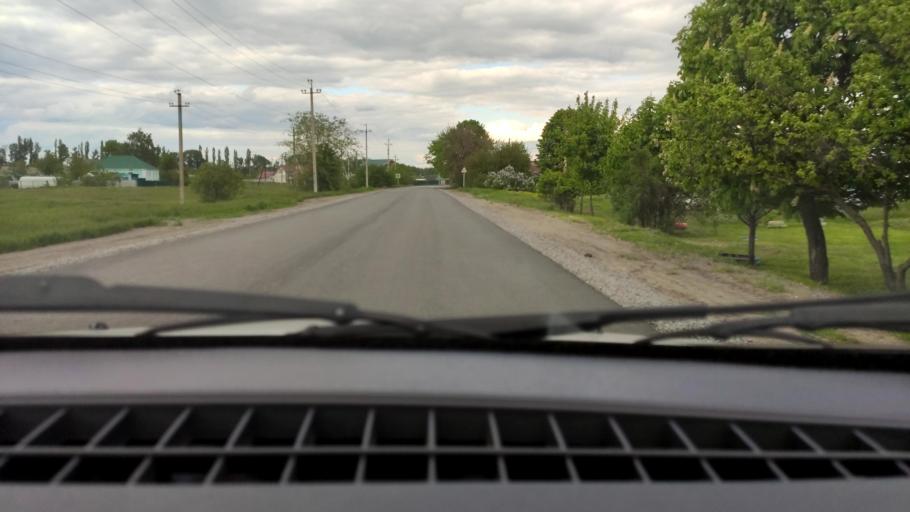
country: RU
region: Voronezj
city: Podkletnoye
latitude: 51.5881
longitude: 39.4622
